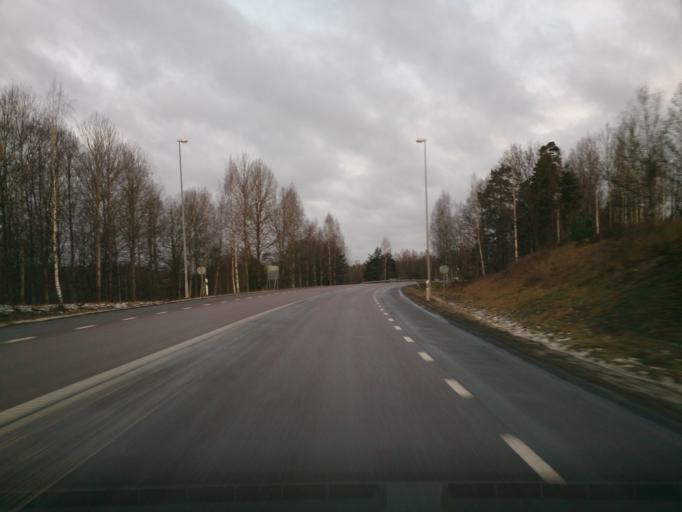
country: SE
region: OEstergoetland
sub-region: Atvidabergs Kommun
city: Atvidaberg
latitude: 58.2153
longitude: 15.9771
